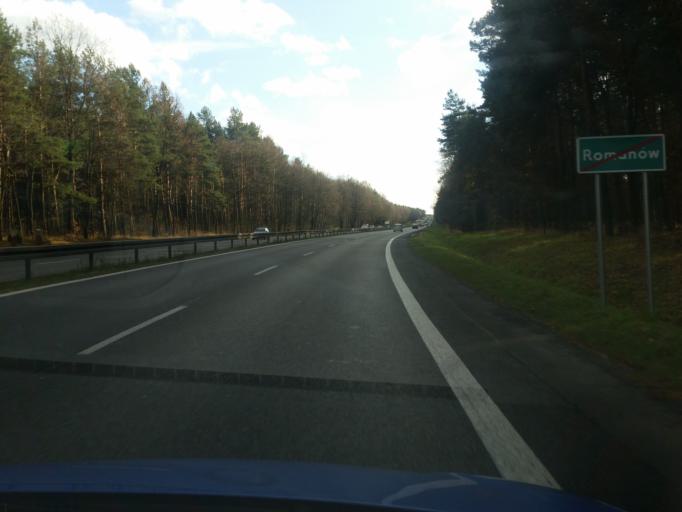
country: PL
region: Silesian Voivodeship
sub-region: Powiat czestochowski
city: Kamienica Polska
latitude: 50.6600
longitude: 19.1295
